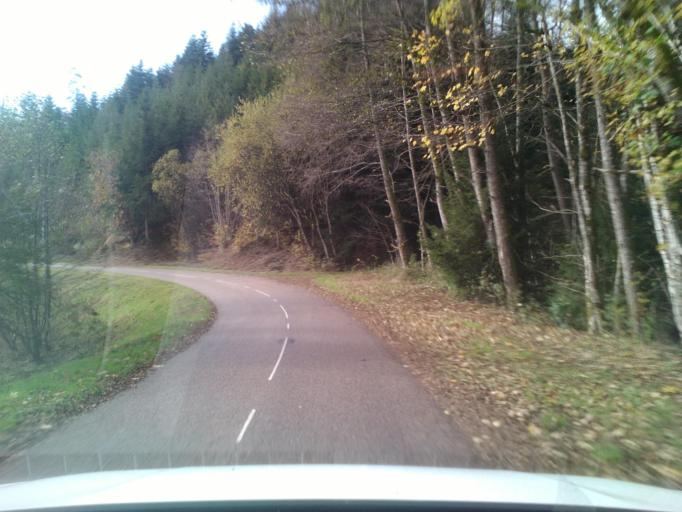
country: FR
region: Lorraine
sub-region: Departement des Vosges
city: Senones
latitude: 48.4057
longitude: 7.0214
